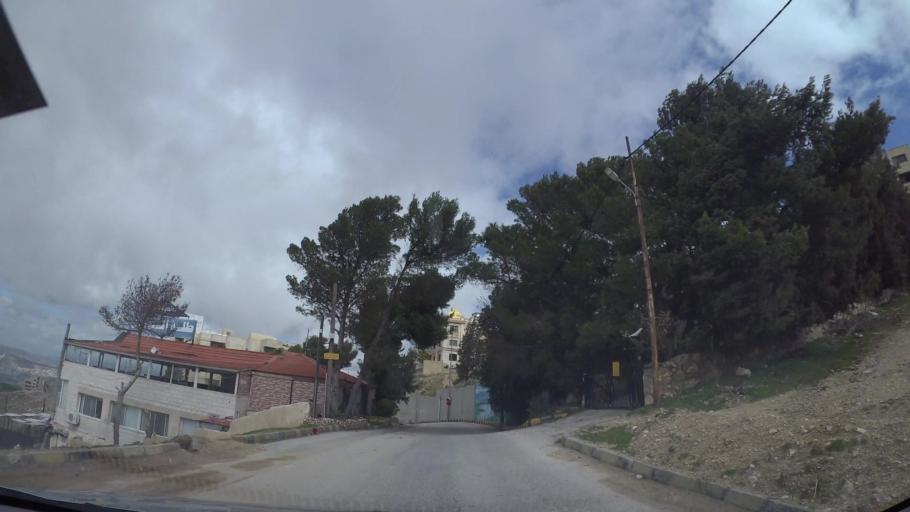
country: JO
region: Amman
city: Al Jubayhah
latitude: 32.0483
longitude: 35.8721
